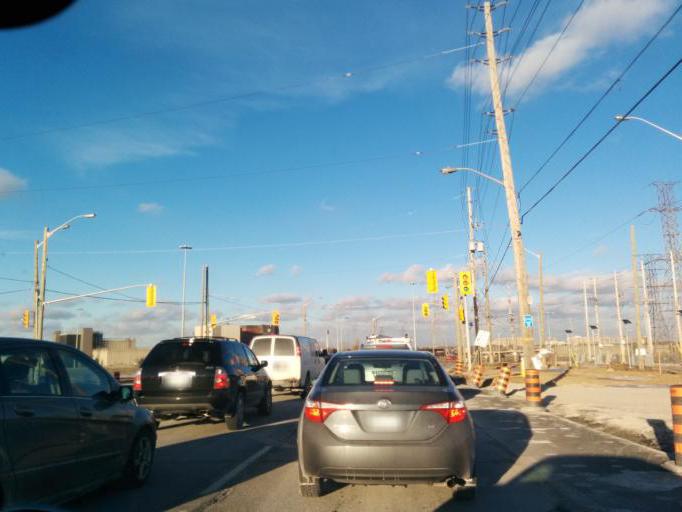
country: CA
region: Ontario
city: Etobicoke
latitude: 43.6680
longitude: -79.5866
